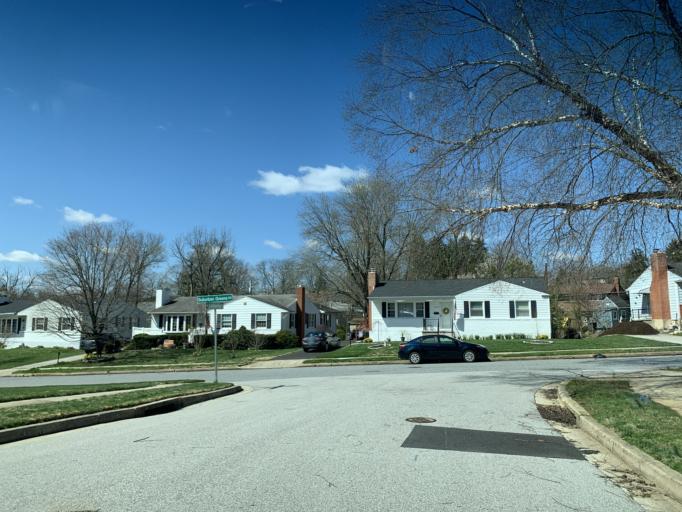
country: US
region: Maryland
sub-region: Baltimore County
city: Timonium
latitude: 39.4437
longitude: -76.6094
